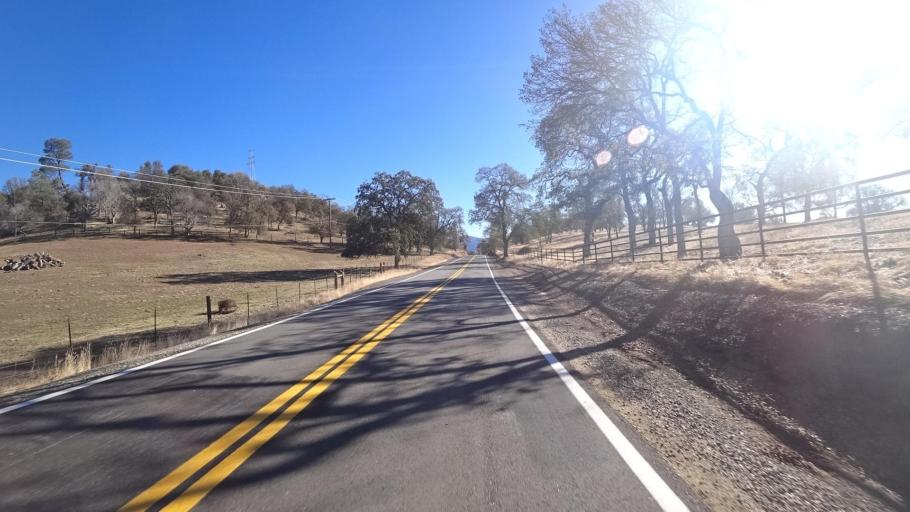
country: US
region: California
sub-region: Kern County
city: Alta Sierra
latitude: 35.7055
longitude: -118.7548
